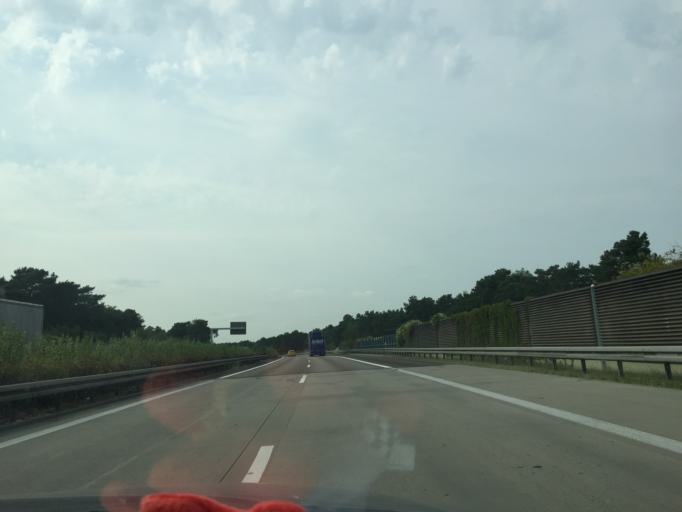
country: DE
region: Brandenburg
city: Schwerin
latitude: 52.1654
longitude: 13.6417
